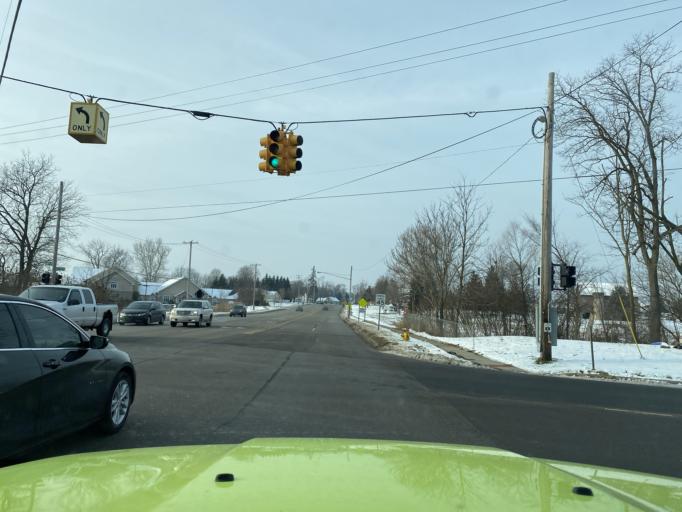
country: US
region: Michigan
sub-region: Ottawa County
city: Hudsonville
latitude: 42.8871
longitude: -85.8716
